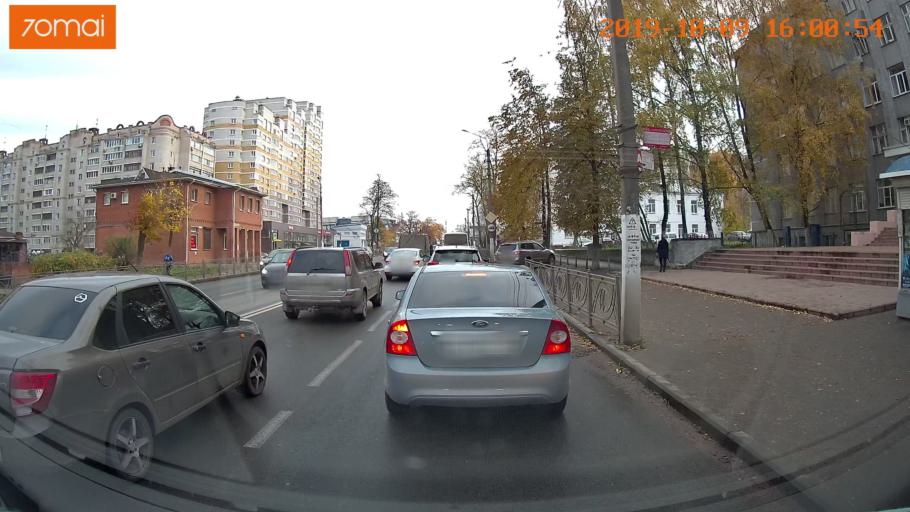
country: RU
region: Kostroma
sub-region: Kostromskoy Rayon
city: Kostroma
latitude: 57.7656
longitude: 40.9511
